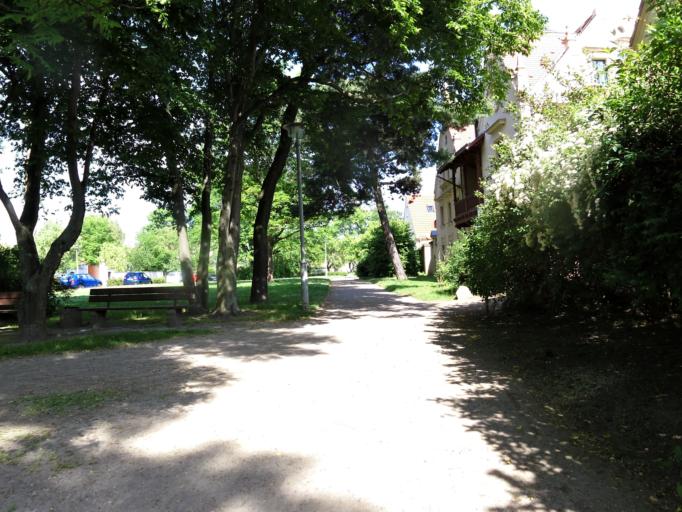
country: DE
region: Saxony
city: Leipzig
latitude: 51.3062
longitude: 12.4278
